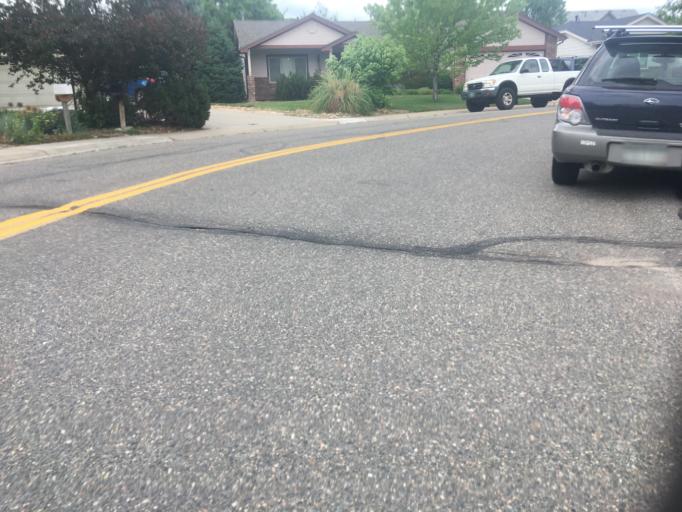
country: US
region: Colorado
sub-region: Boulder County
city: Louisville
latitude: 39.9968
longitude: -105.1223
